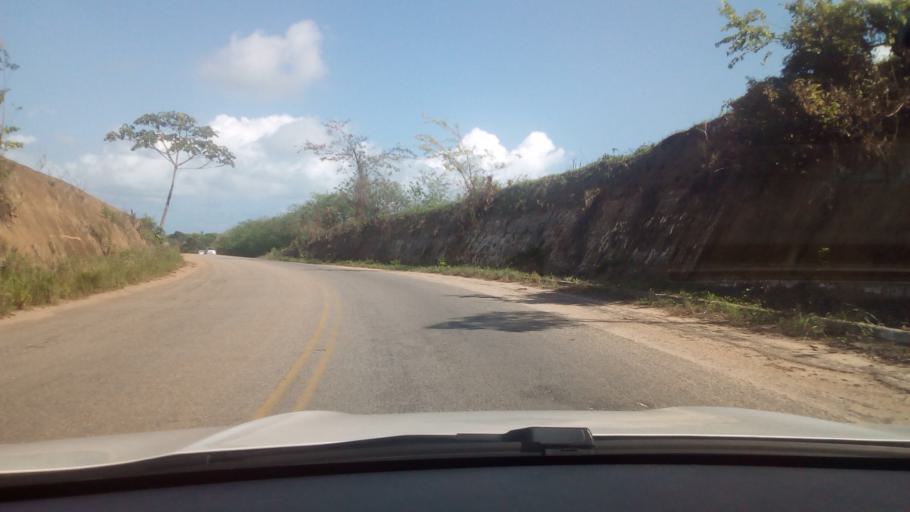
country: BR
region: Paraiba
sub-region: Conde
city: Conde
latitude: -7.2388
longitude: -34.8432
